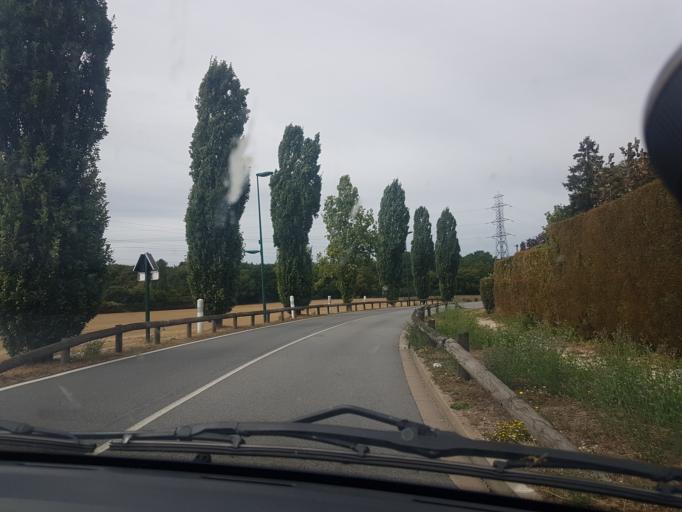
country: FR
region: Ile-de-France
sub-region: Departement des Yvelines
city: Plaisir
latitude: 48.8072
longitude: 1.9466
